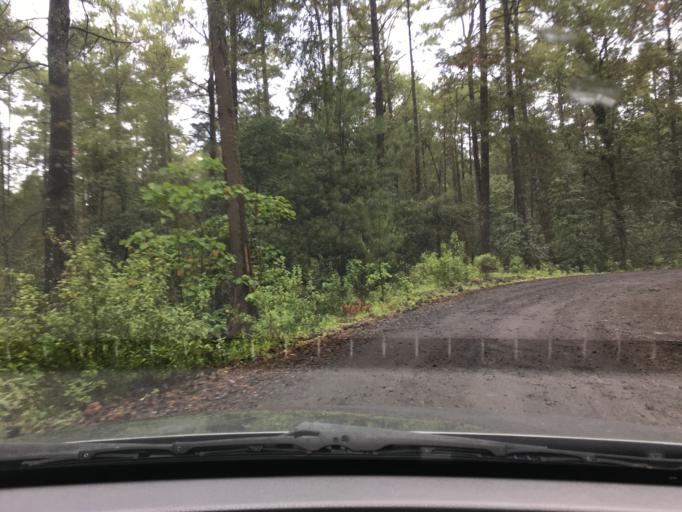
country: MX
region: Michoacan
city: Nuevo San Juan Parangaricutiro
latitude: 19.4495
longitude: -102.1855
